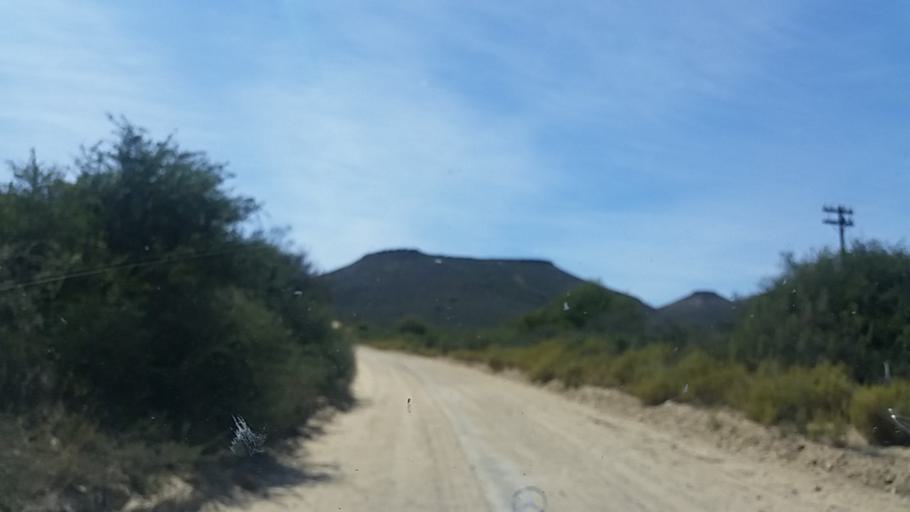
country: ZA
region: Western Cape
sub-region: Eden District Municipality
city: Knysna
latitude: -33.6392
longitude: 23.1468
